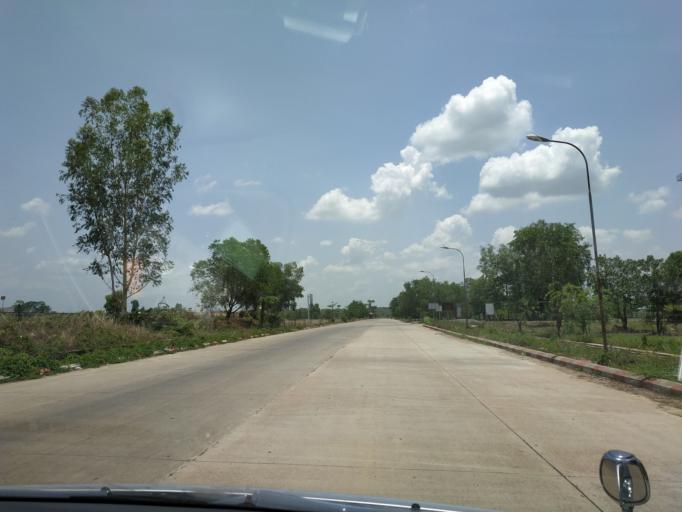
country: MM
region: Bago
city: Bago
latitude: 17.4676
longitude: 96.4522
